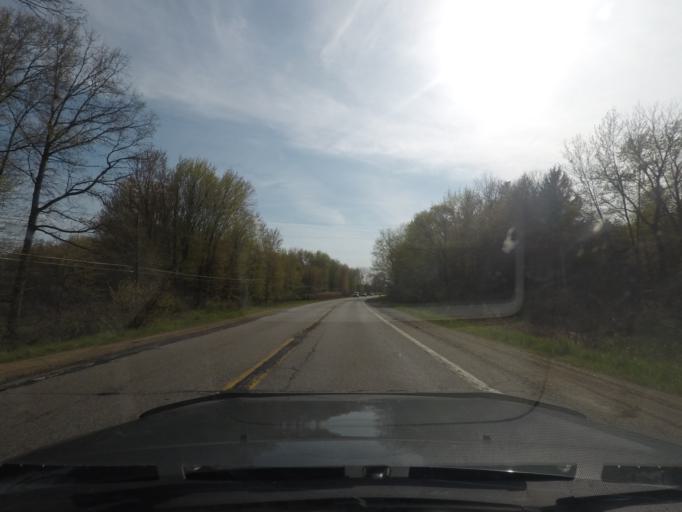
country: US
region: Michigan
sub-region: Berrien County
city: Buchanan
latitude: 41.7948
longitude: -86.4189
